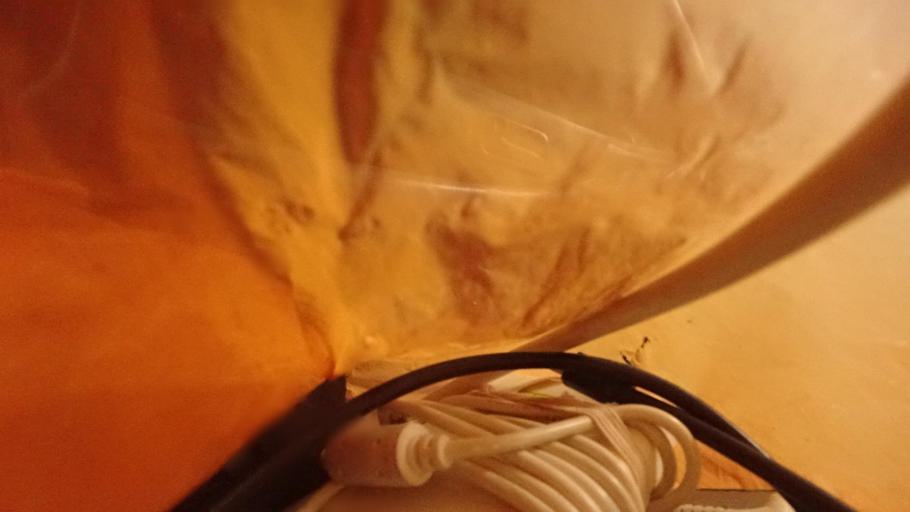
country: RU
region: Jewish Autonomous Oblast
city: Khingansk
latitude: 49.0146
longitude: 131.0596
